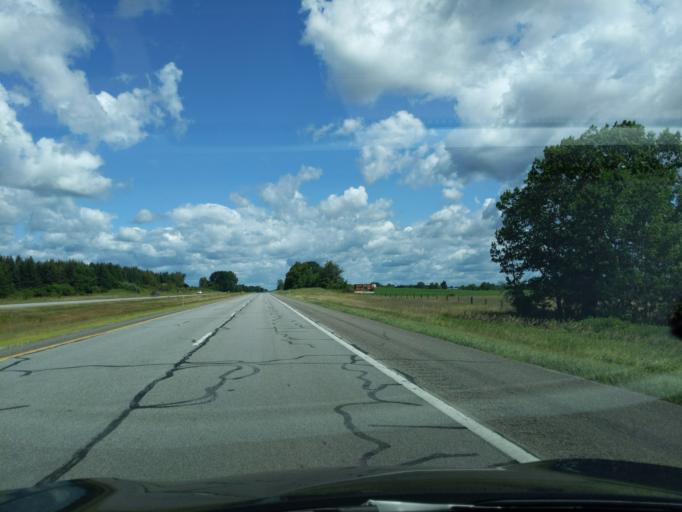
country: US
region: Michigan
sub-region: Clare County
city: Clare
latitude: 43.7625
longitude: -84.7582
